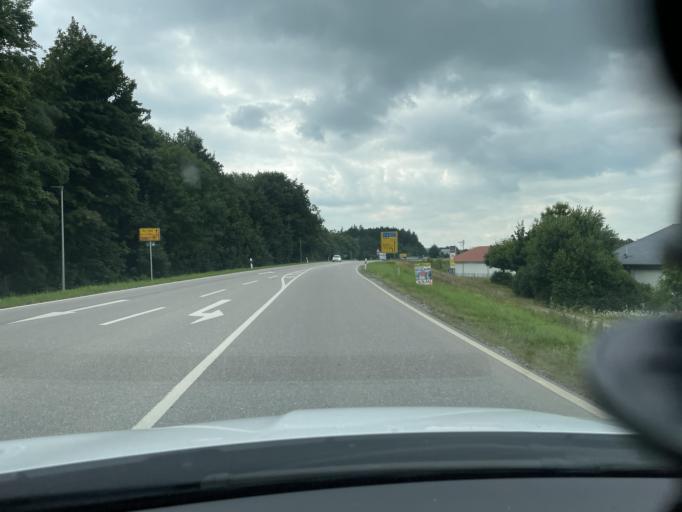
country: DE
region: Bavaria
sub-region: Upper Bavaria
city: Haag in Oberbayern
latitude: 48.1634
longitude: 12.1672
